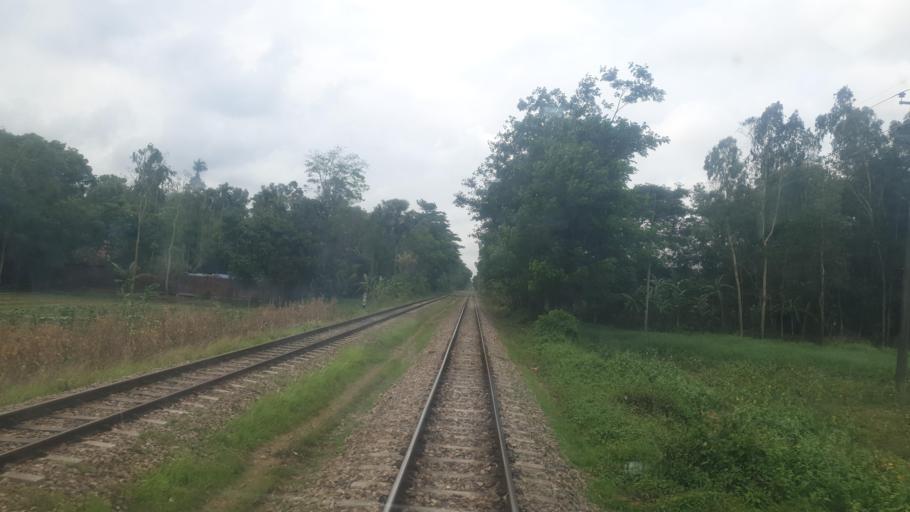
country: BD
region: Chittagong
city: Fatikchari
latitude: 22.6427
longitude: 91.6512
